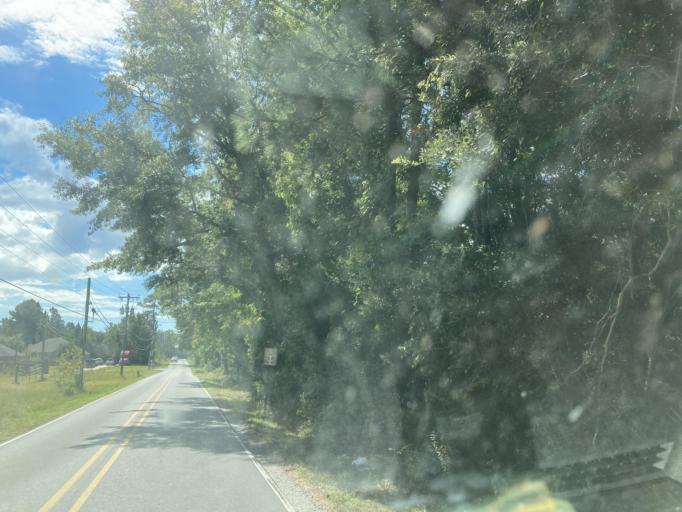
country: US
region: Mississippi
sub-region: Jackson County
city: Saint Martin
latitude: 30.4424
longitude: -88.8665
